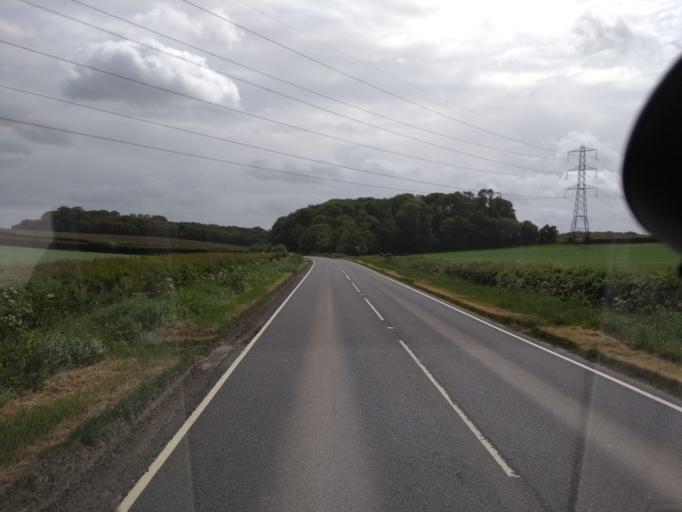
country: GB
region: England
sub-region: Somerset
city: Bridgwater
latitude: 51.1775
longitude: -3.0967
